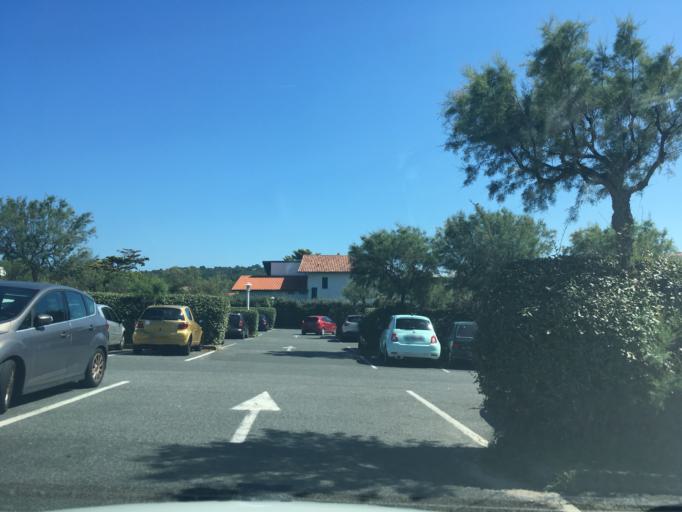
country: FR
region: Aquitaine
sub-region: Departement des Pyrenees-Atlantiques
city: Biarritz
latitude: 43.4617
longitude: -1.5764
